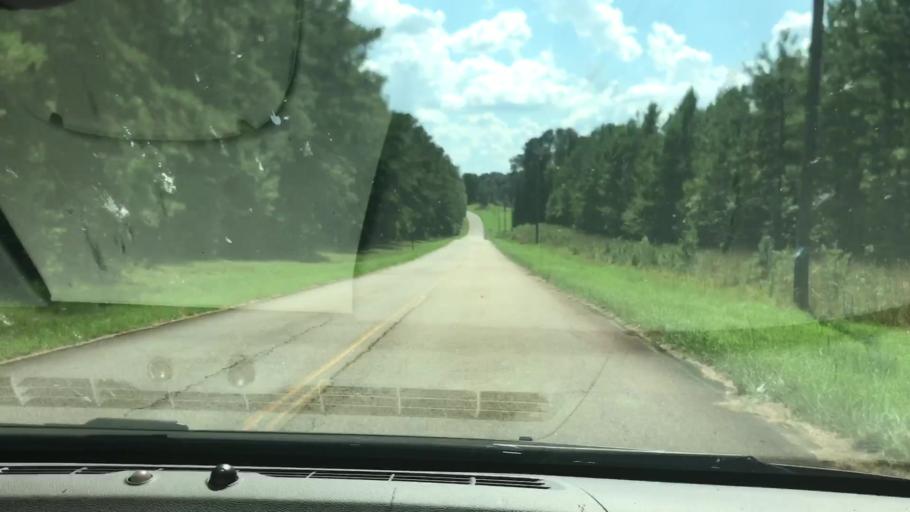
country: US
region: Georgia
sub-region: Troup County
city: La Grange
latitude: 33.1140
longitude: -85.1252
